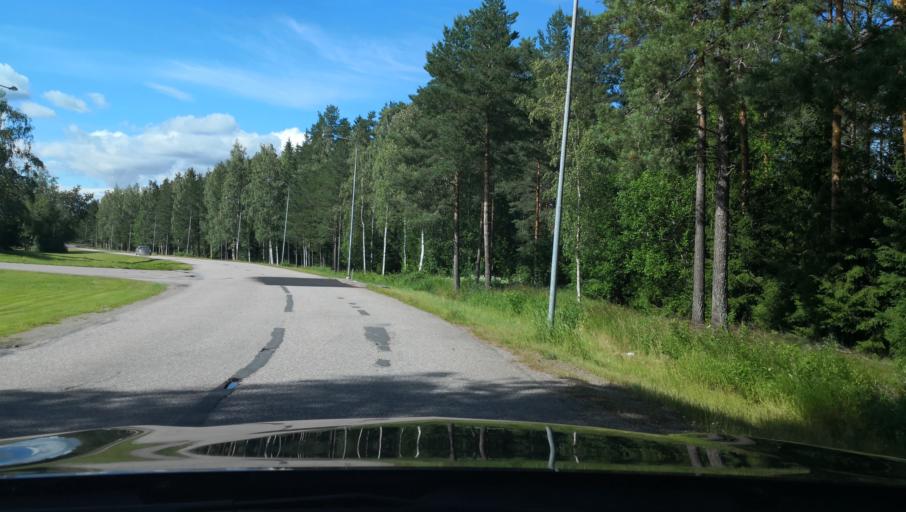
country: SE
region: Vaestmanland
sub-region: Surahammars Kommun
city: Surahammar
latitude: 59.6935
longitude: 16.2445
